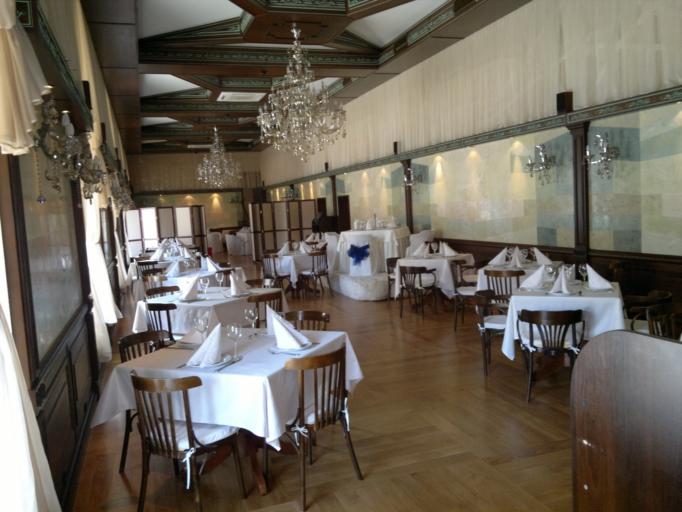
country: RU
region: St.-Petersburg
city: Centralniy
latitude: 59.9460
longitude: 30.3890
